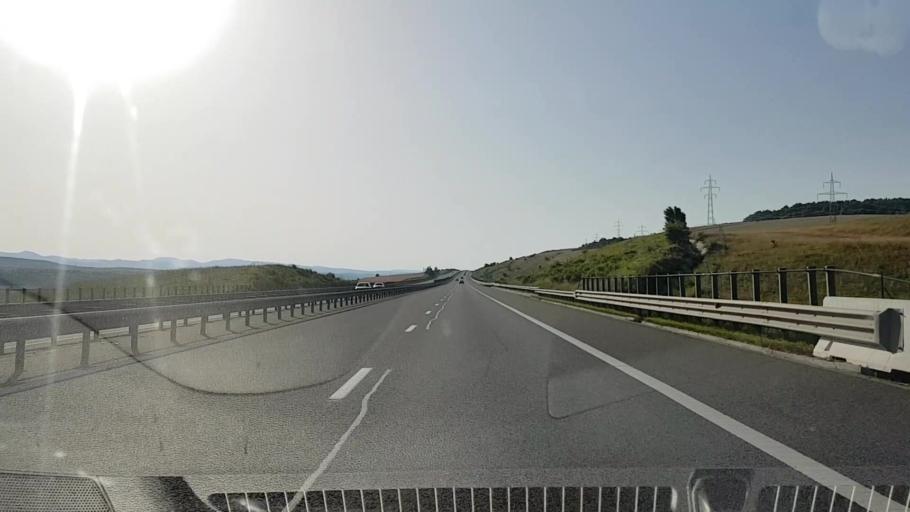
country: RO
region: Cluj
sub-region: Comuna Petrestii De Jos
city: Petrestii de Jos
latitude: 46.6047
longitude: 23.6133
